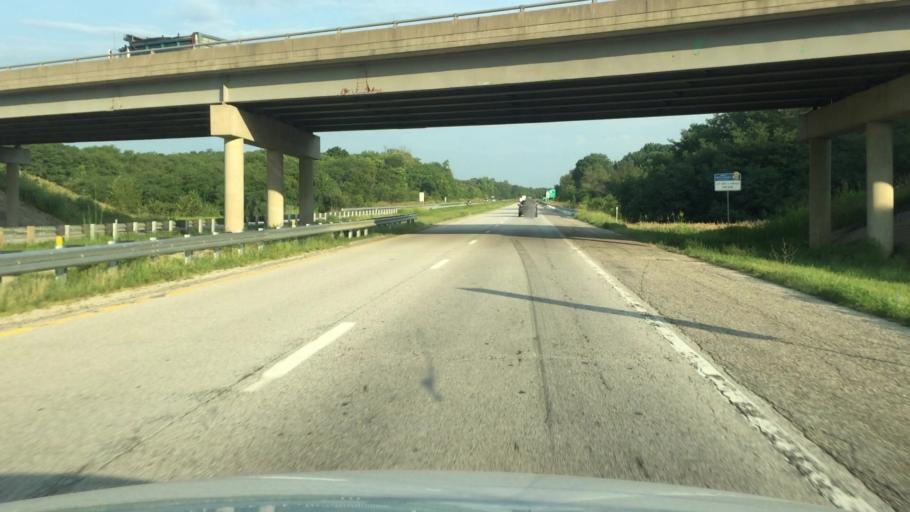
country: US
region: Missouri
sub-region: Buchanan County
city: Saint Joseph
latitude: 39.7168
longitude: -94.8201
